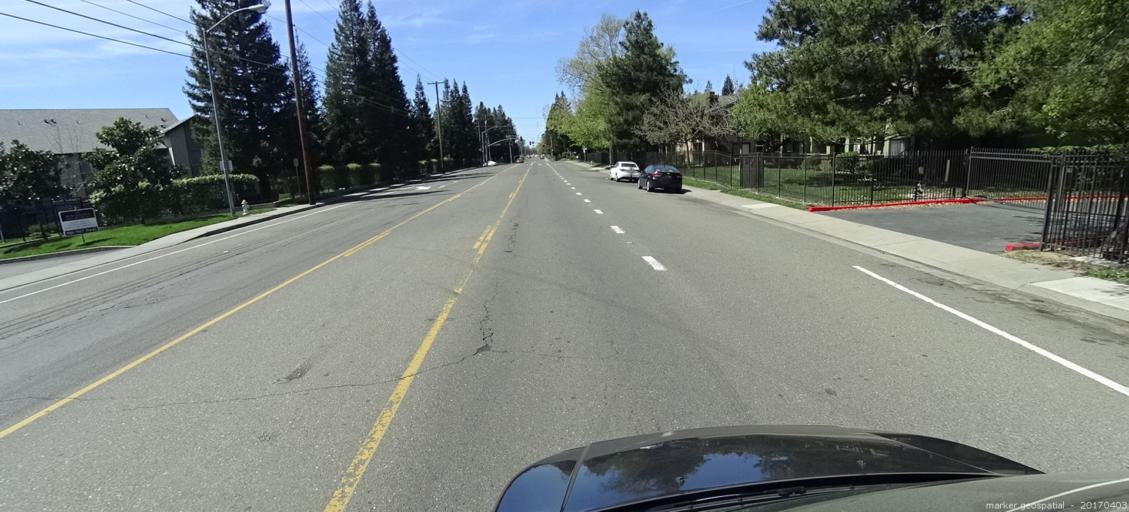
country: US
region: California
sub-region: Sacramento County
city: Rio Linda
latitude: 38.6477
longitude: -121.4548
